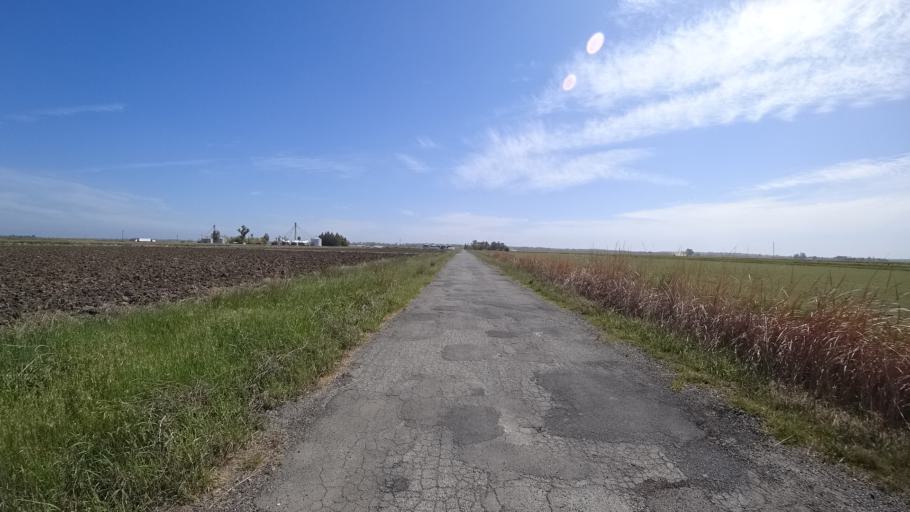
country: US
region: California
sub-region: Glenn County
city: Hamilton City
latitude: 39.5799
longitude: -122.0337
